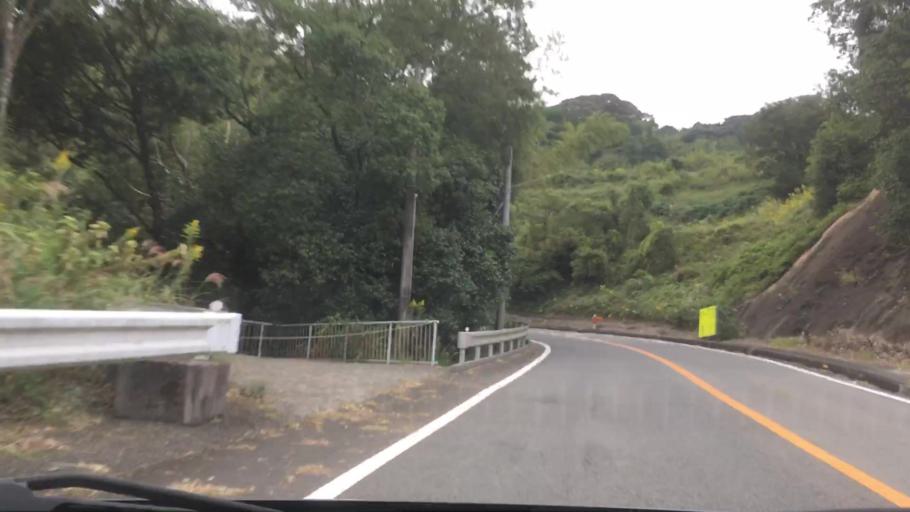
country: JP
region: Nagasaki
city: Sasebo
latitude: 32.9984
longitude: 129.7268
